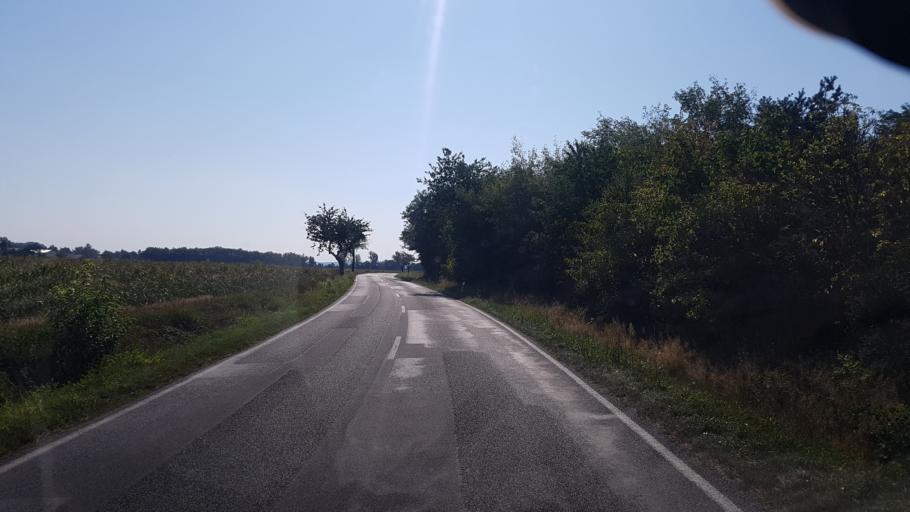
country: DE
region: Brandenburg
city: Hirschfeld
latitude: 51.3948
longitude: 13.6020
